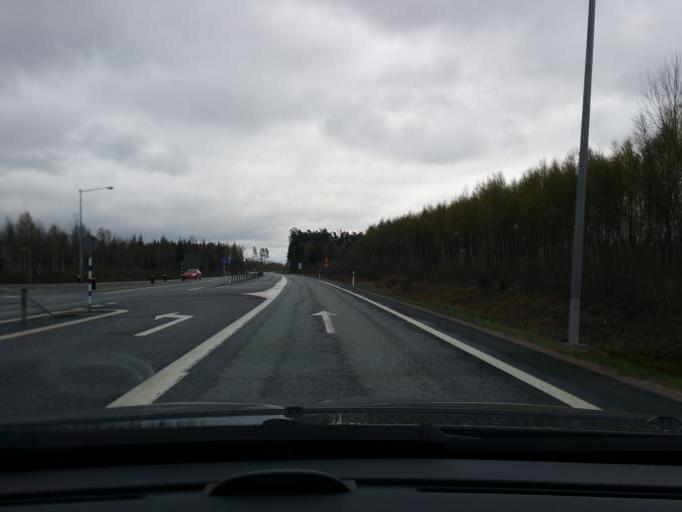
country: SE
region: Kronoberg
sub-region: Vaxjo Kommun
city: Vaexjoe
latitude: 56.9111
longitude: 14.7215
